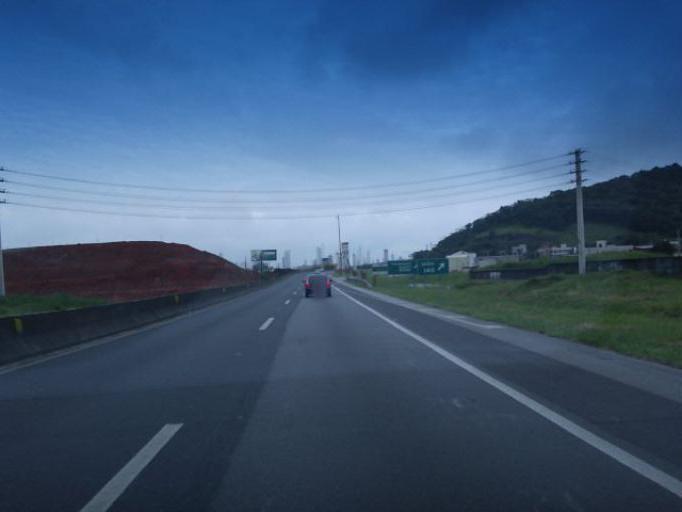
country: BR
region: Santa Catarina
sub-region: Balneario Camboriu
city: Balneario Camboriu
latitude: -27.0340
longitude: -48.6047
